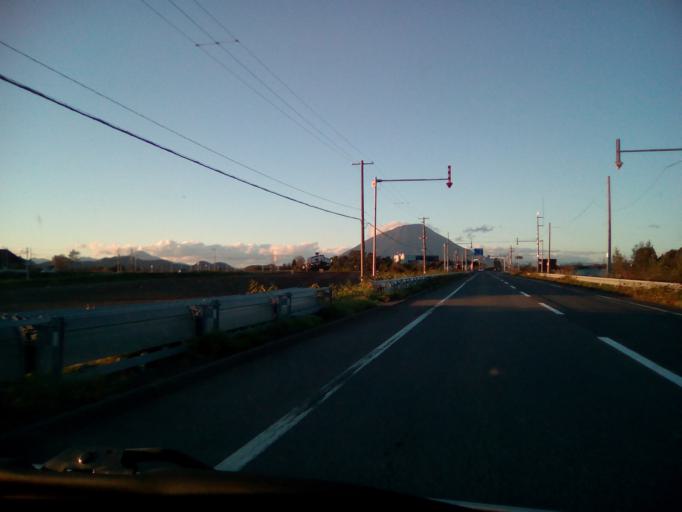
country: JP
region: Hokkaido
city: Niseko Town
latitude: 42.6600
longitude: 140.8118
